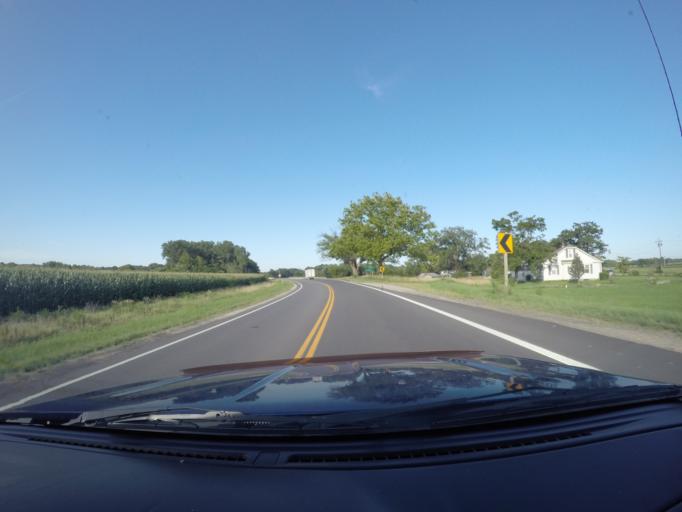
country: US
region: Kansas
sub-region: Douglas County
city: Lawrence
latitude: 39.0009
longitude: -95.1926
